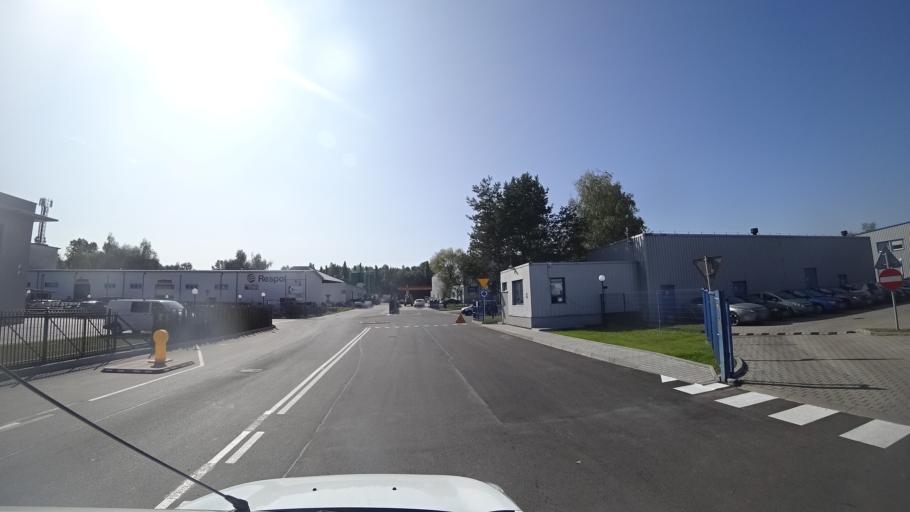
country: PL
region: Lesser Poland Voivodeship
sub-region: Krakow
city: Sidzina
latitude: 50.0057
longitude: 19.9004
